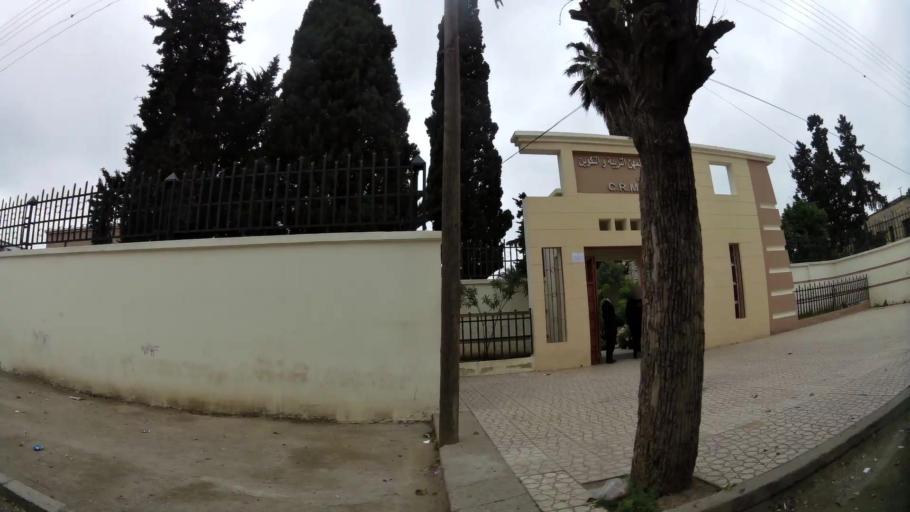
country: MA
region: Fes-Boulemane
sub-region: Fes
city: Fes
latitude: 34.0460
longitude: -4.9982
